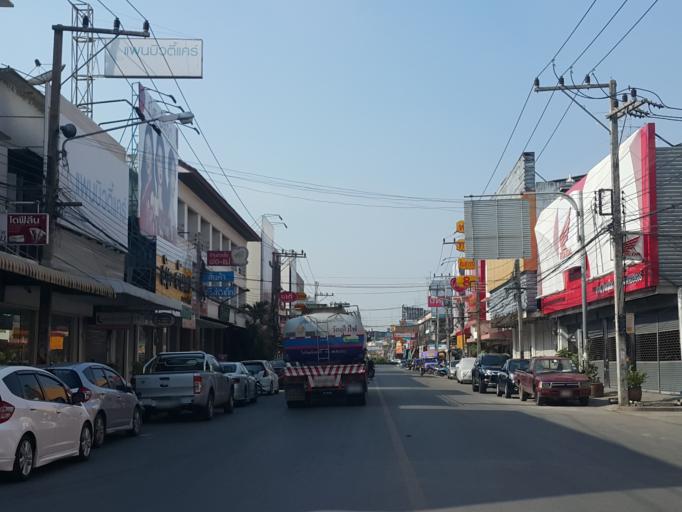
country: TH
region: Phitsanulok
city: Phitsanulok
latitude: 16.8128
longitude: 100.2644
